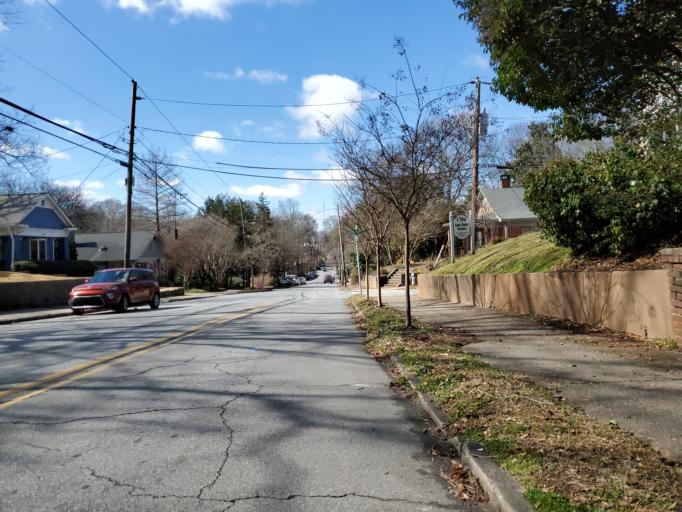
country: US
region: Georgia
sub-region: DeKalb County
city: Druid Hills
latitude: 33.7649
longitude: -84.3315
